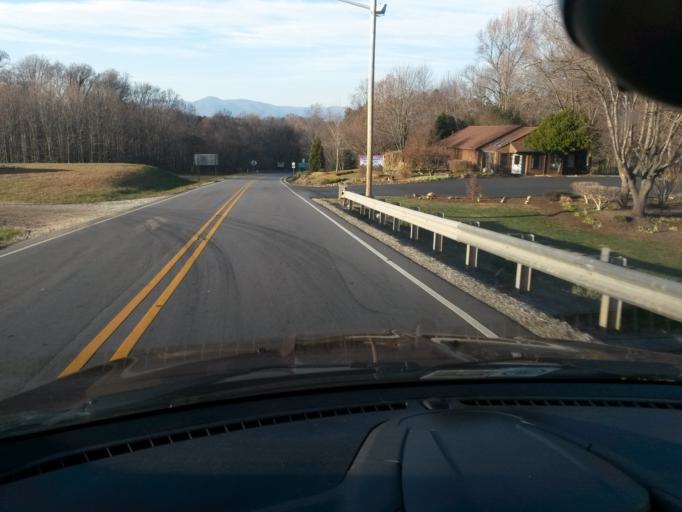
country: US
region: Virginia
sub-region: Amherst County
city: Amherst
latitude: 37.5896
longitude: -79.0508
